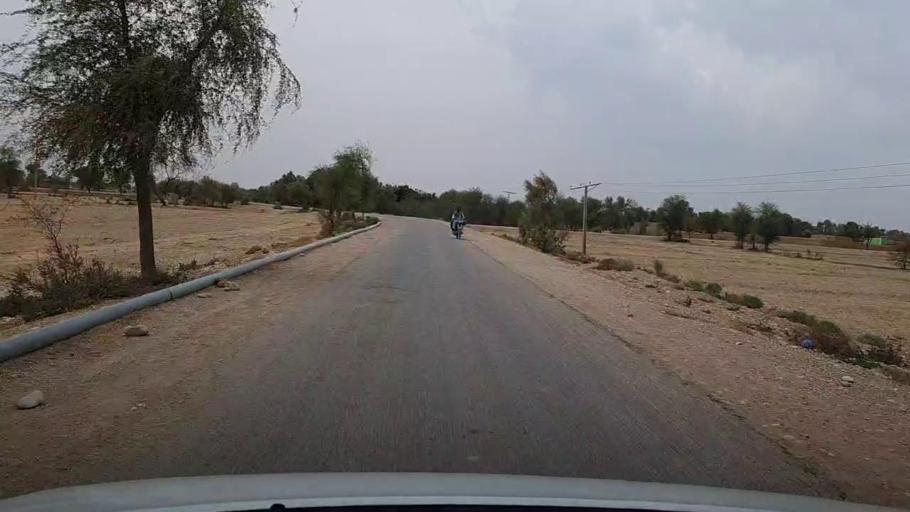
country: PK
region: Sindh
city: Sehwan
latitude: 26.3212
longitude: 67.7317
